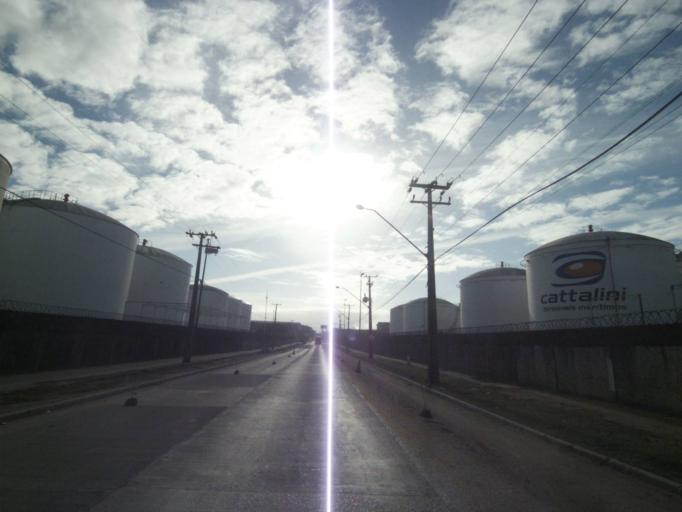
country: BR
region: Parana
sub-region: Paranagua
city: Paranagua
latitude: -25.5110
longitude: -48.5322
